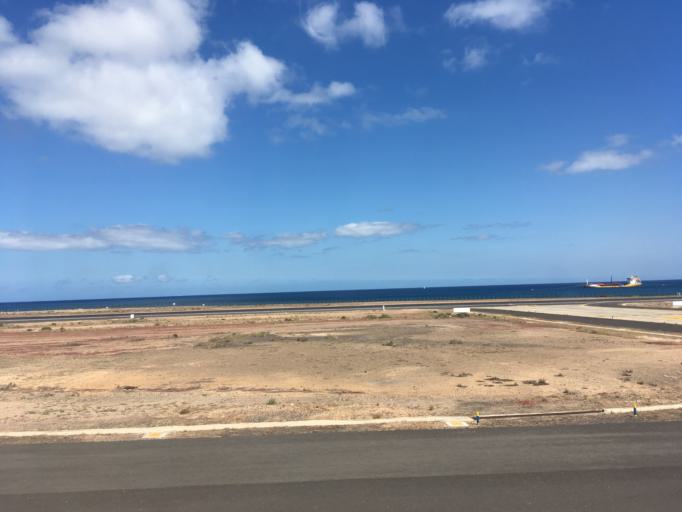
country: ES
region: Canary Islands
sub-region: Provincia de Las Palmas
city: Tias
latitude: 28.9446
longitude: -13.6078
